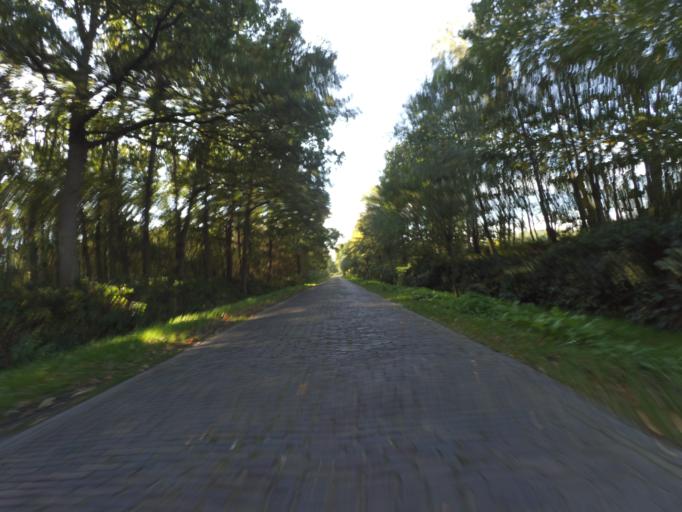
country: NL
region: Gelderland
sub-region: Gemeente Nijkerk
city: Nijkerk
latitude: 52.2449
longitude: 5.5315
